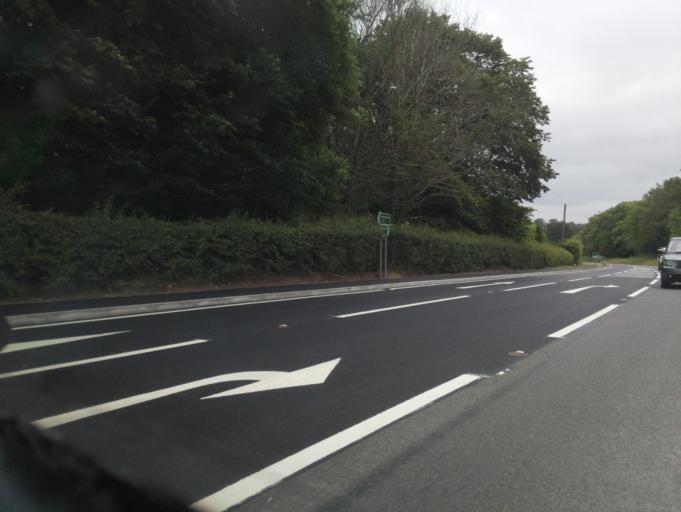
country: GB
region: England
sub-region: Derbyshire
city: Yeldersley
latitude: 52.9746
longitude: -1.6475
